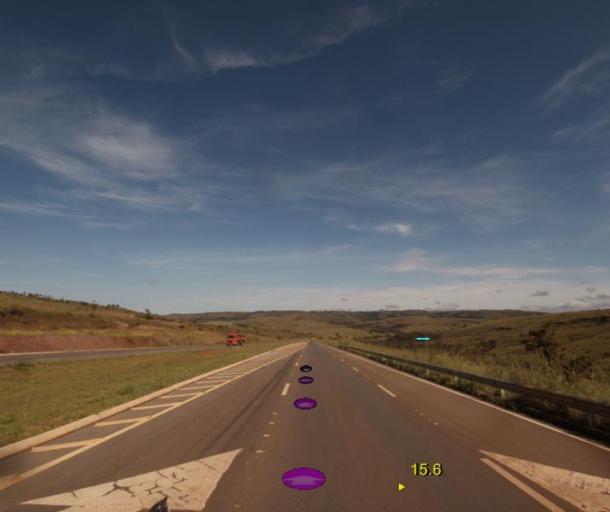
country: BR
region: Federal District
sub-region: Brasilia
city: Brasilia
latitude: -15.7552
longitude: -48.3383
